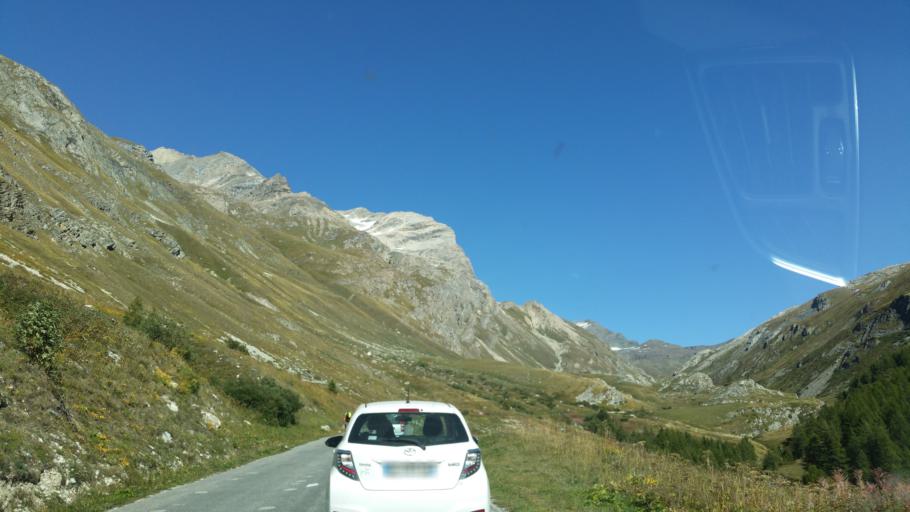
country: FR
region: Rhone-Alpes
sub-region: Departement de la Savoie
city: Val-d'Isere
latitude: 45.4517
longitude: 7.0147
